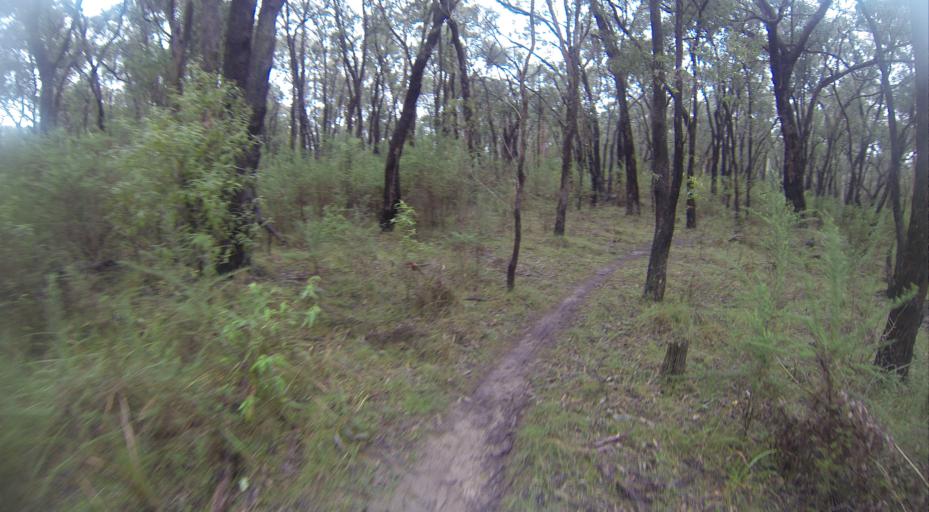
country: AU
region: Victoria
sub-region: Yarra Ranges
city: Belgrave South
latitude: -37.9324
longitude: 145.3269
